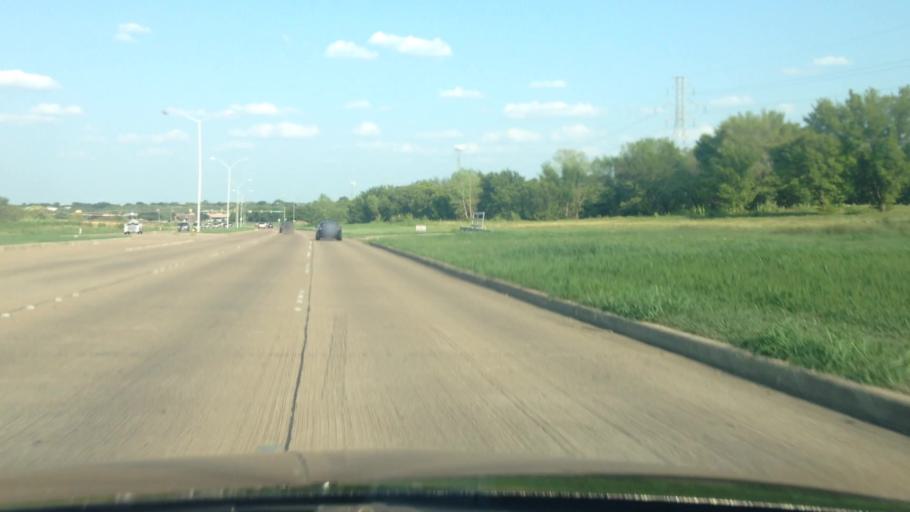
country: US
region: Texas
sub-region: Tarrant County
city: Edgecliff Village
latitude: 32.6484
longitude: -97.3445
